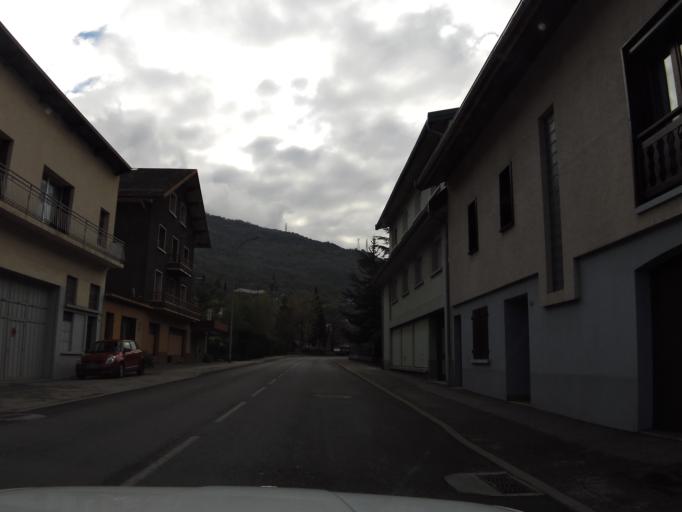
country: FR
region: Rhone-Alpes
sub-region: Departement de la Savoie
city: Saint-Michel-de-Maurienne
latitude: 45.2195
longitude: 6.4679
